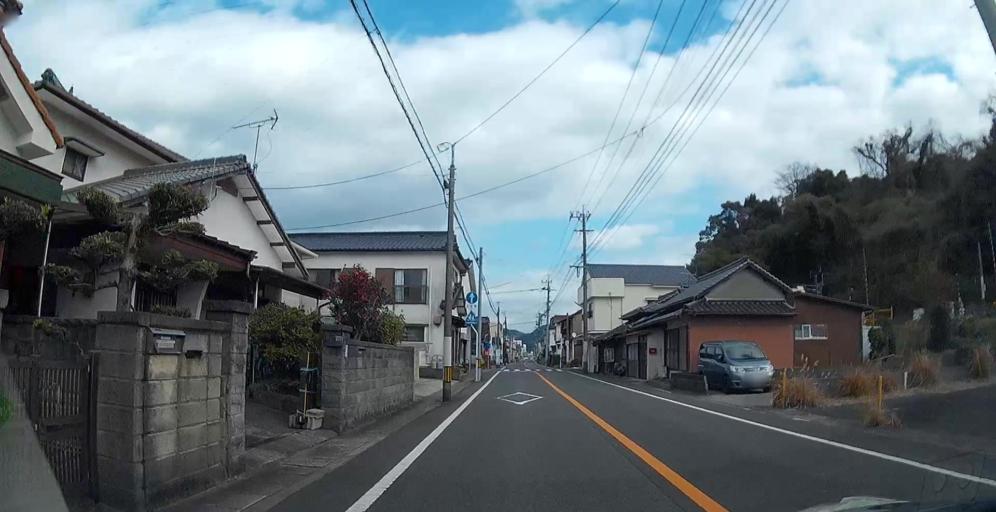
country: JP
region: Kumamoto
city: Minamata
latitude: 32.2022
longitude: 130.3914
